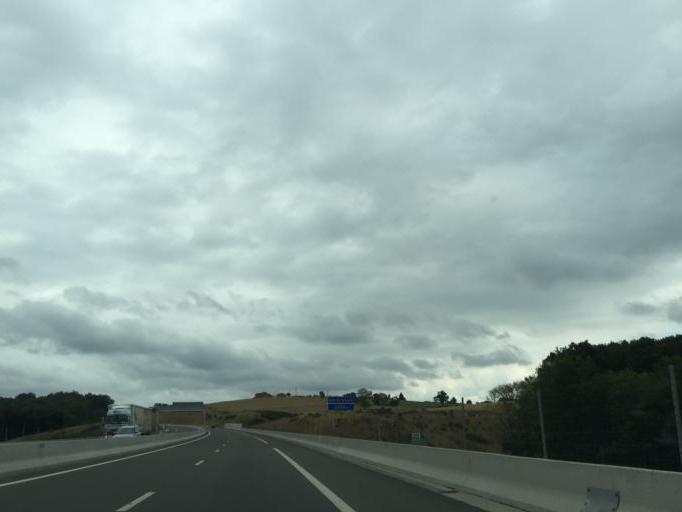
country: FR
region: Rhone-Alpes
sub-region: Departement de la Loire
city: Balbigny
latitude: 45.8396
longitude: 4.1989
